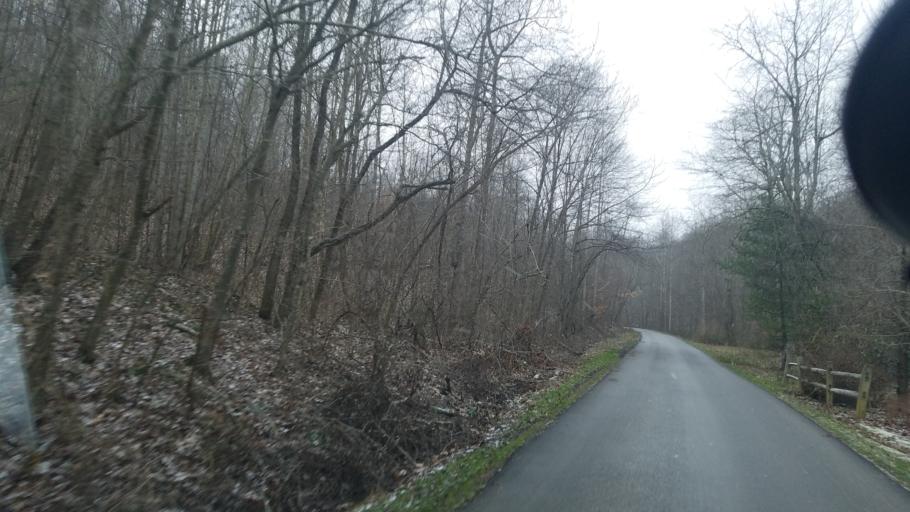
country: US
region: Kentucky
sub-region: Lewis County
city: Vanceburg
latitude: 38.4774
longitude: -83.5058
